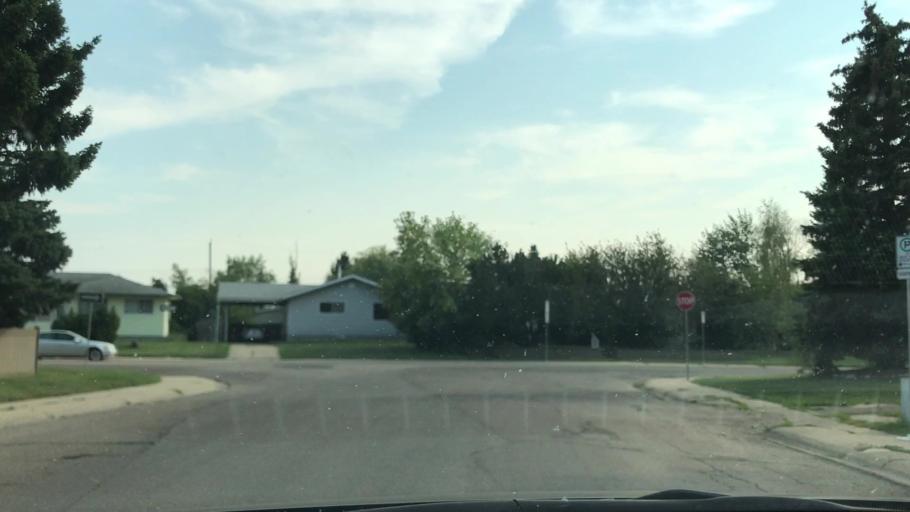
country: CA
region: Alberta
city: Edmonton
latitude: 53.4899
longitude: -113.5119
